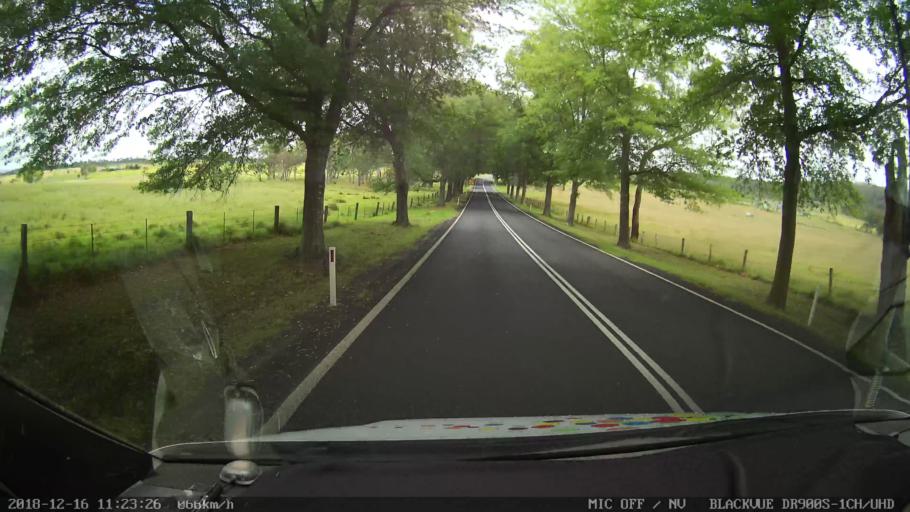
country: AU
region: New South Wales
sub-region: Tenterfield Municipality
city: Carrolls Creek
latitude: -29.0541
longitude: 152.0357
